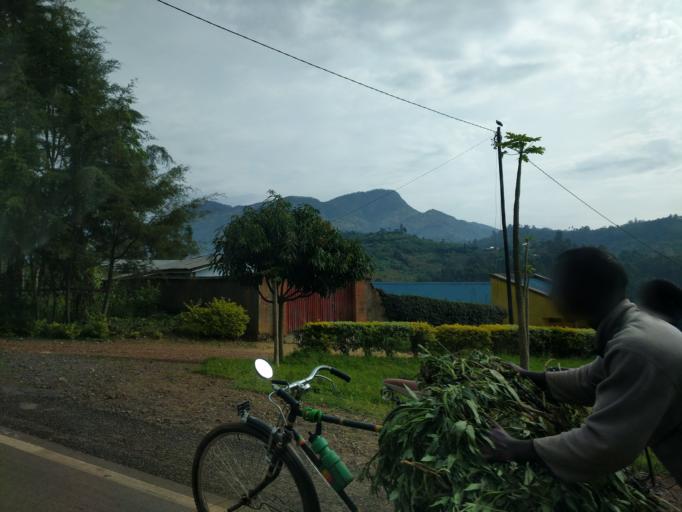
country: RW
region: Northern Province
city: Musanze
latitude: -1.6467
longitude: 29.7865
